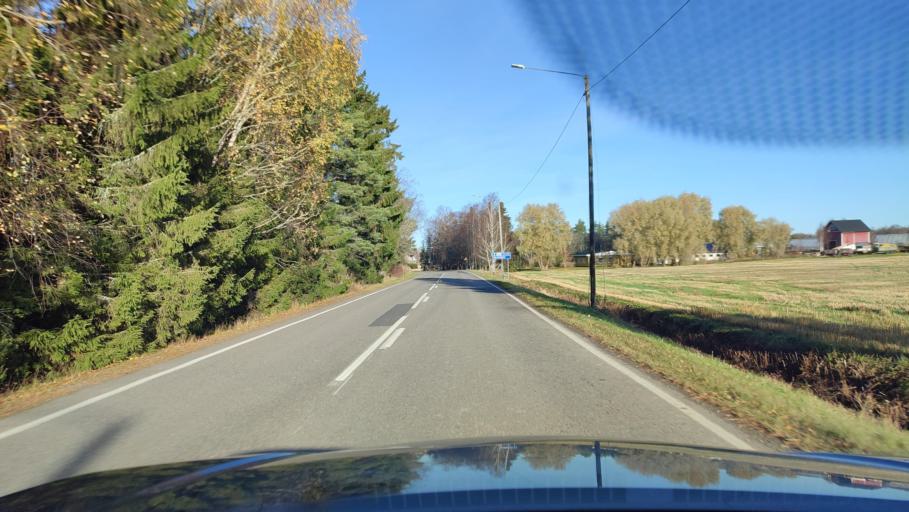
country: FI
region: Southern Ostrobothnia
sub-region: Suupohja
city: Teuva
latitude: 62.4650
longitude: 21.7141
